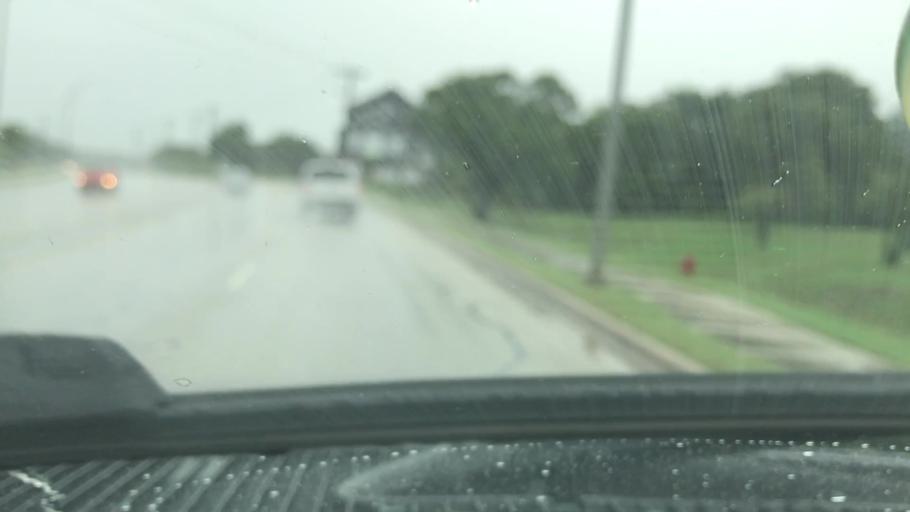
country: US
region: Texas
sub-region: Williamson County
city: Cedar Park
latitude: 30.4968
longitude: -97.8209
